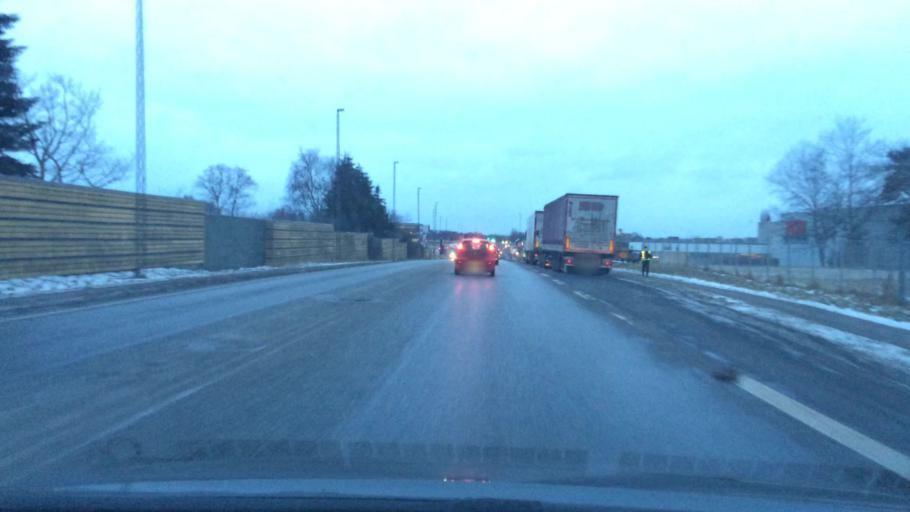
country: DK
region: Central Jutland
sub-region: Horsens Kommune
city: Horsens
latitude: 55.8352
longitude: 9.8097
